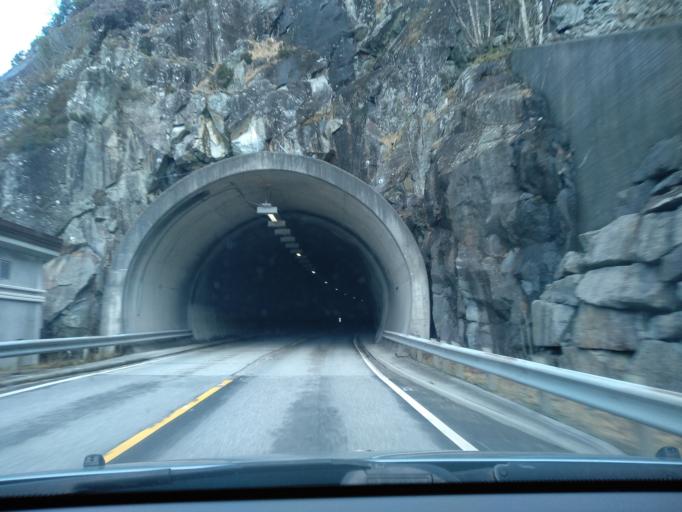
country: NO
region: Rogaland
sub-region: Sauda
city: Sauda
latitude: 59.8634
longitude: 6.3609
